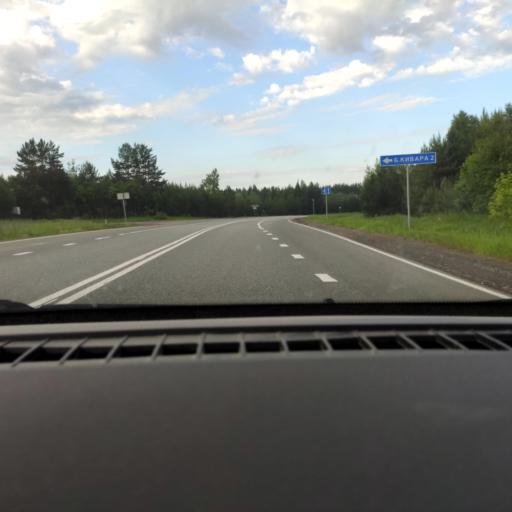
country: RU
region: Udmurtiya
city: Votkinsk
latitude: 57.1749
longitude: 54.1558
